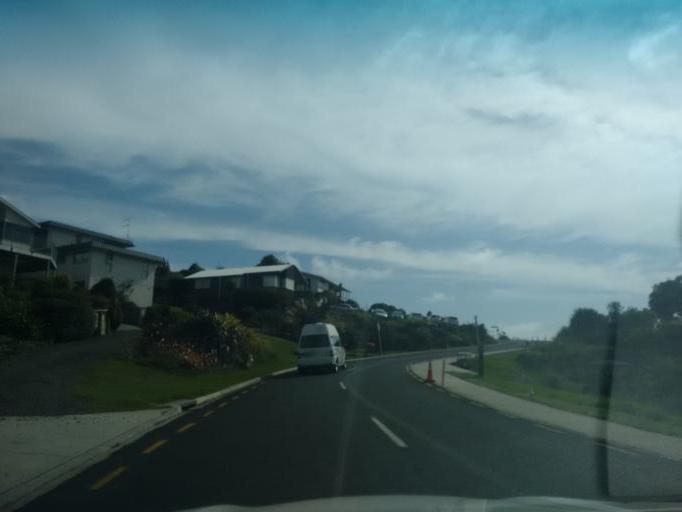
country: NZ
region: Waikato
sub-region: Thames-Coromandel District
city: Whitianga
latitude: -36.8380
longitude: 175.8004
